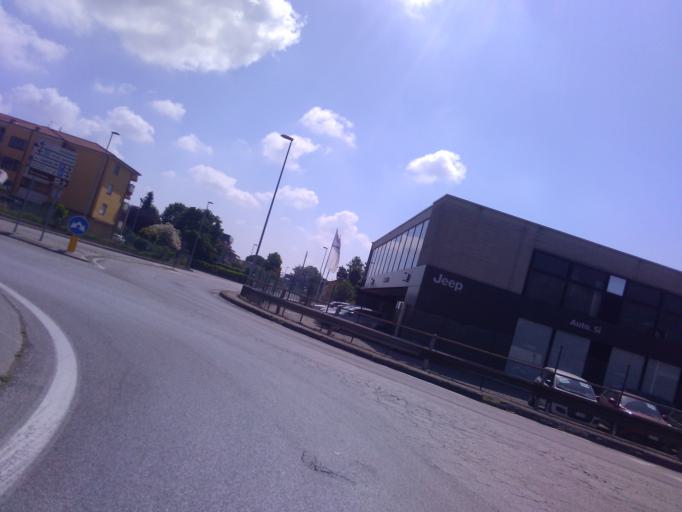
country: IT
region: Tuscany
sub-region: Provincia di Lucca
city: Lucca
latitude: 43.8405
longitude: 10.4764
